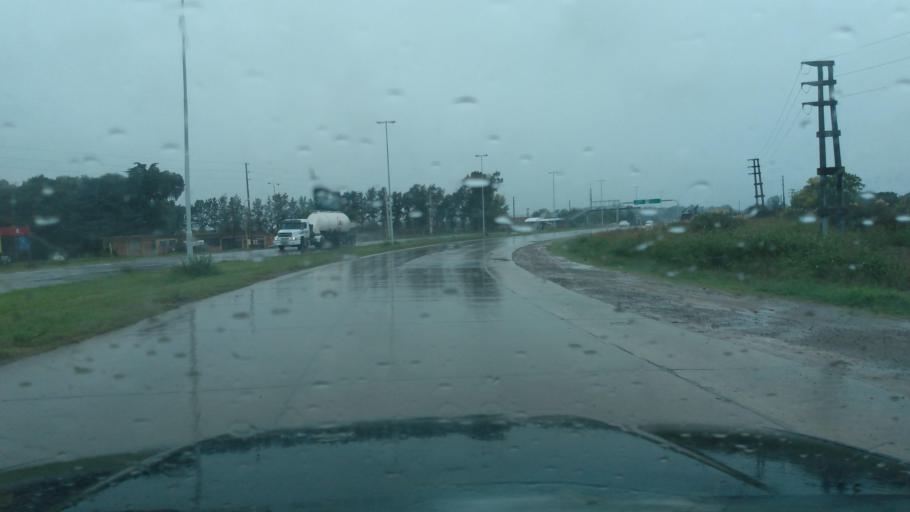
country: AR
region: Buenos Aires
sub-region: Partido de Campana
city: Campana
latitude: -34.2040
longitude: -58.9592
